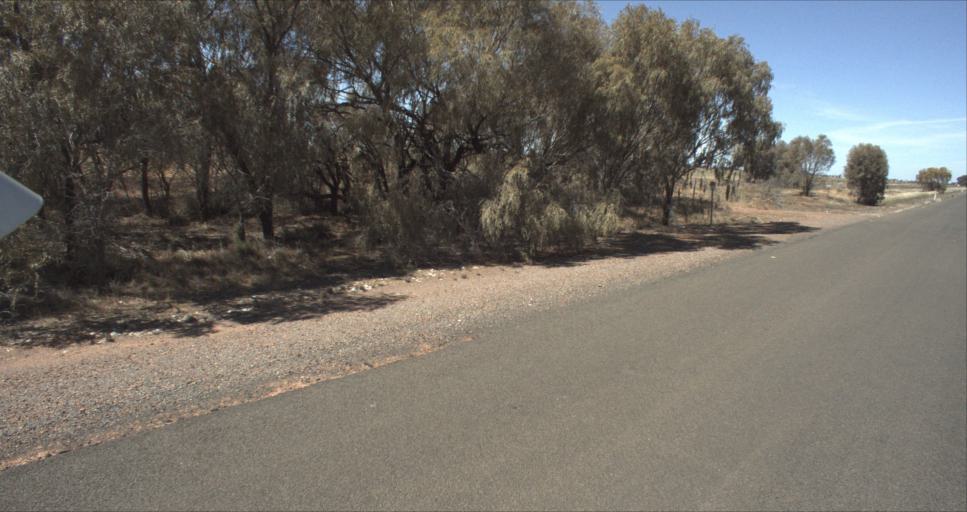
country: AU
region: New South Wales
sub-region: Leeton
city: Leeton
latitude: -34.4869
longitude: 146.2895
